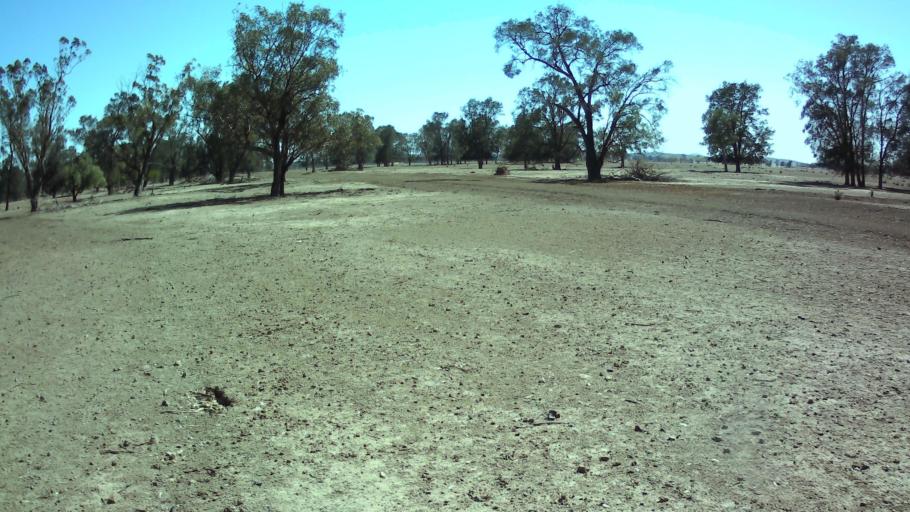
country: AU
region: New South Wales
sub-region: Bland
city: West Wyalong
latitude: -33.7651
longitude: 147.6578
